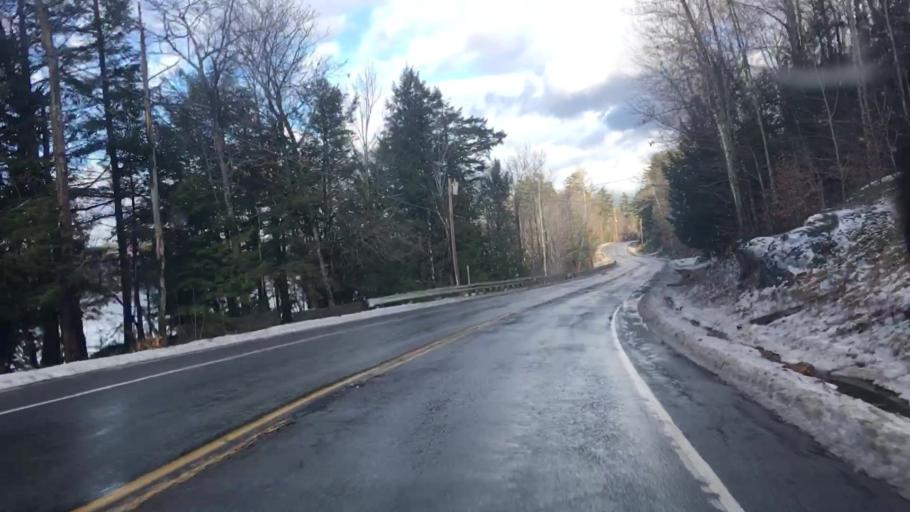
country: US
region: Maine
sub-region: Hancock County
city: Dedham
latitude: 44.6544
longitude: -68.6826
